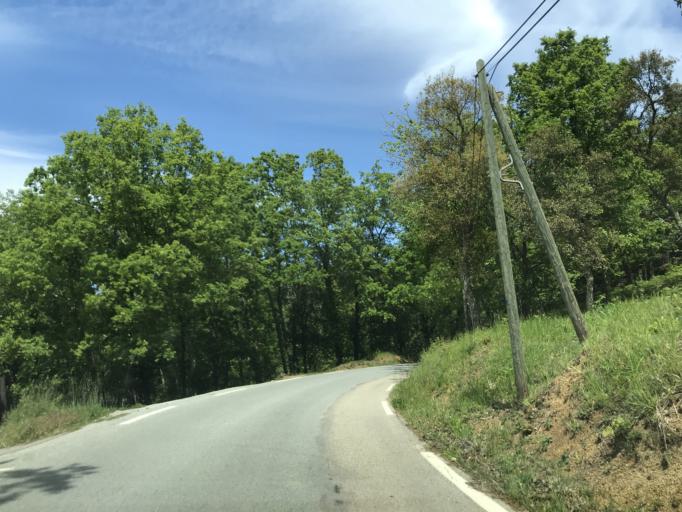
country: FR
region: Provence-Alpes-Cote d'Azur
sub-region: Departement du Var
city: Montauroux
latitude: 43.5855
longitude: 6.8165
